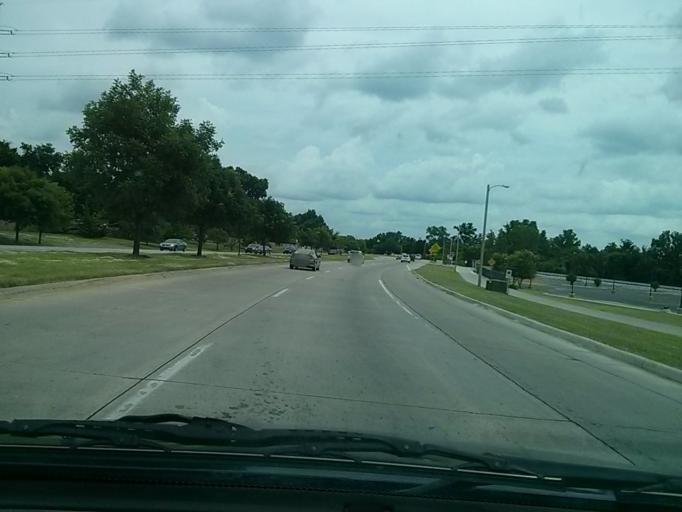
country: US
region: Oklahoma
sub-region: Tulsa County
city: Jenks
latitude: 36.0384
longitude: -95.9590
